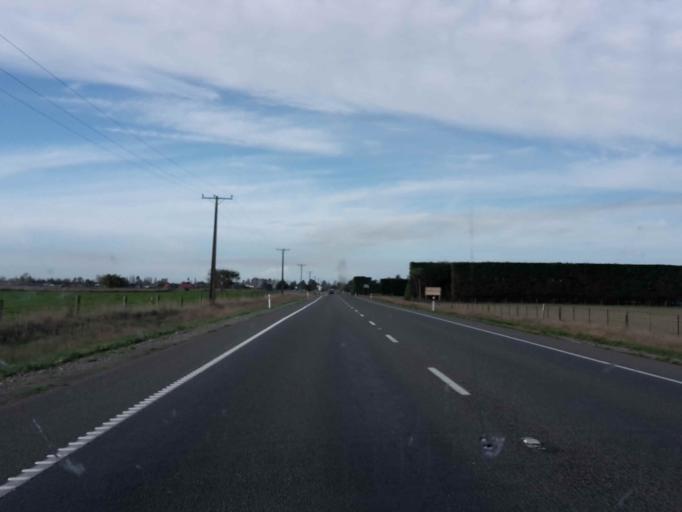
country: NZ
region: Canterbury
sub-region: Ashburton District
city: Tinwald
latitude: -44.0101
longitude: 171.5555
